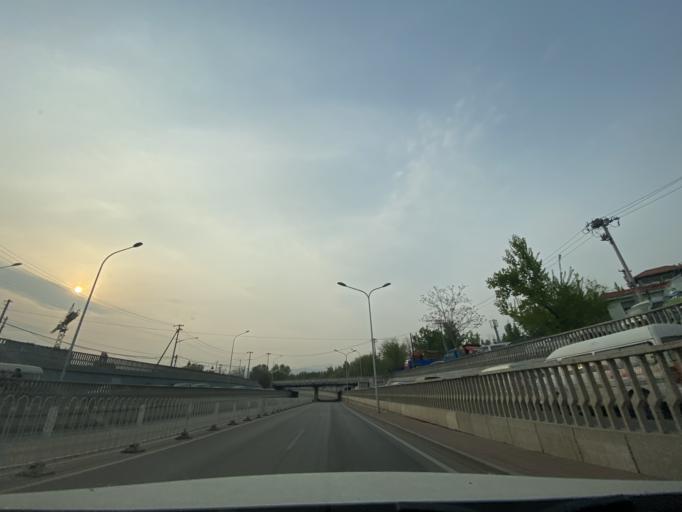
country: CN
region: Beijing
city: Babaoshan
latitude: 39.9301
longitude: 116.2288
